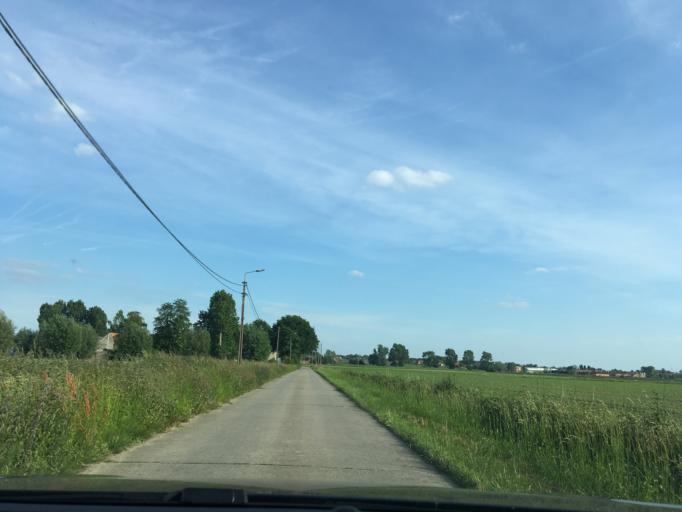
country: BE
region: Flanders
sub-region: Provincie West-Vlaanderen
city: Hooglede
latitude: 50.9573
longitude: 3.0698
